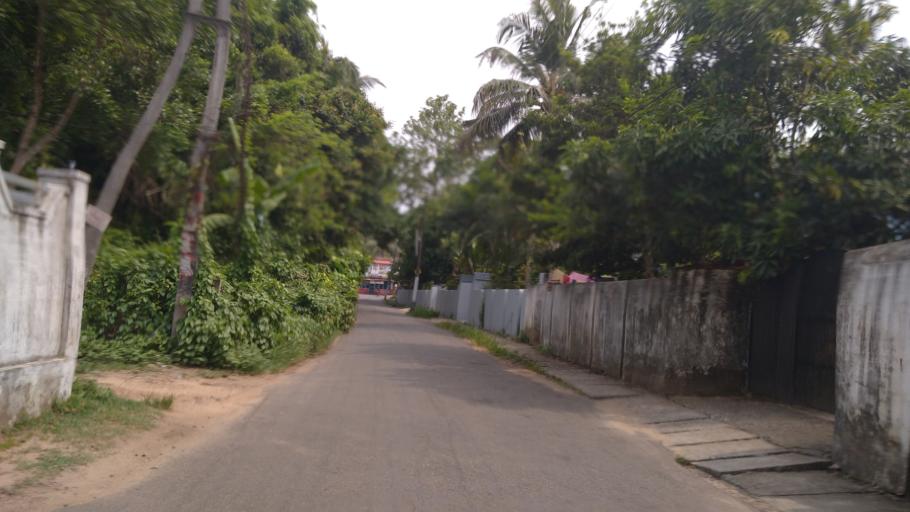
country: IN
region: Kerala
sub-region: Ernakulam
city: Elur
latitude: 10.1473
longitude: 76.2545
